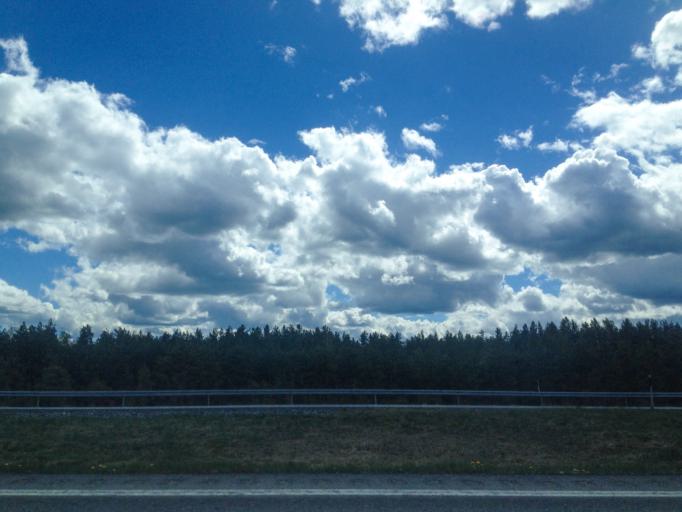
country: FI
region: Haeme
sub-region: Haemeenlinna
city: Kalvola
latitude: 61.1426
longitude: 24.0298
